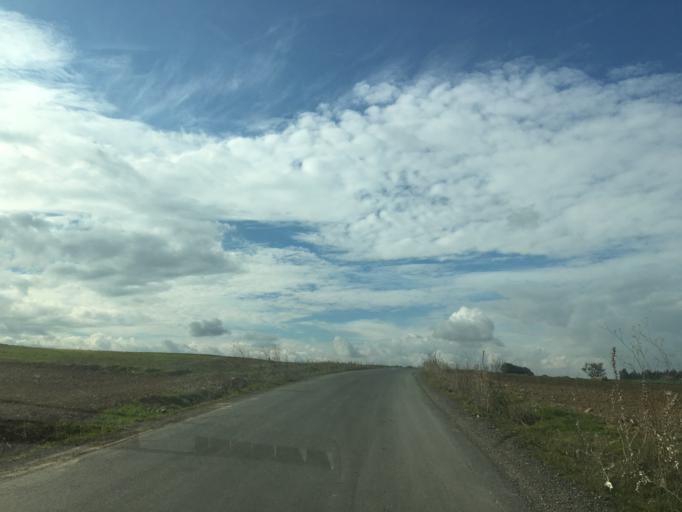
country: DZ
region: Bouira
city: Bouira
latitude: 36.2870
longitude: 3.8604
